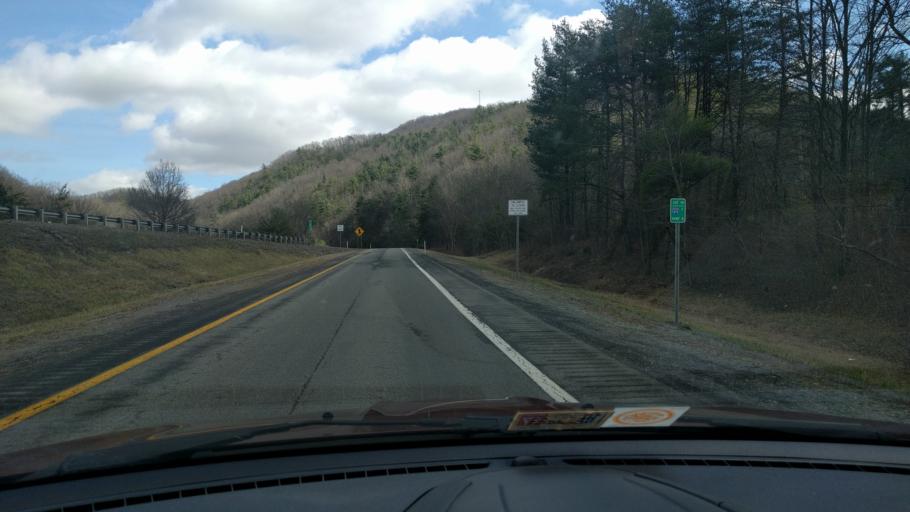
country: US
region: West Virginia
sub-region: Greenbrier County
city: White Sulphur Springs
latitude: 37.7917
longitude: -80.2716
